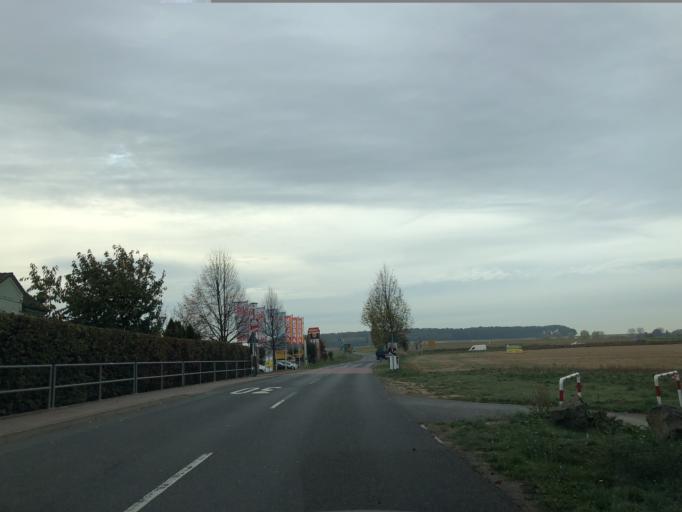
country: DE
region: Hesse
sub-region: Regierungsbezirk Darmstadt
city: Niederdorfelden
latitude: 50.1912
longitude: 8.8030
